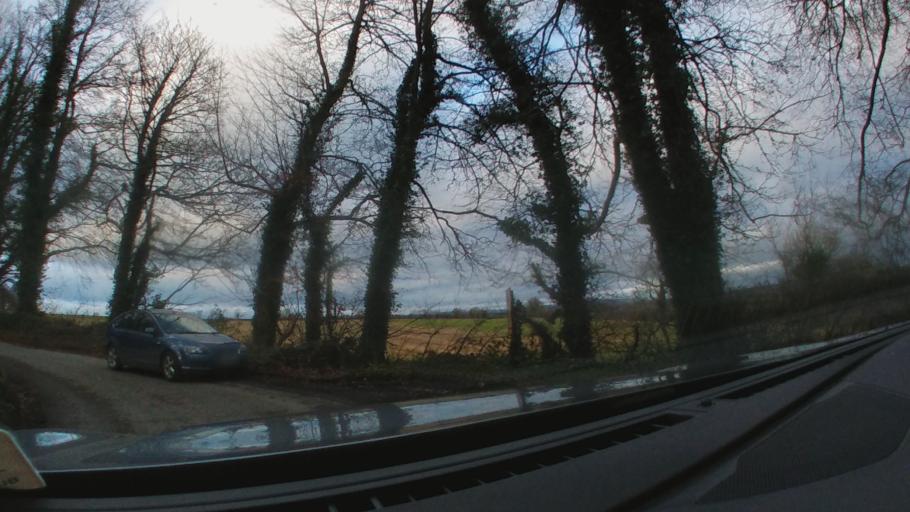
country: IE
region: Leinster
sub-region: Kilkenny
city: Thomastown
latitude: 52.5614
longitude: -7.1362
